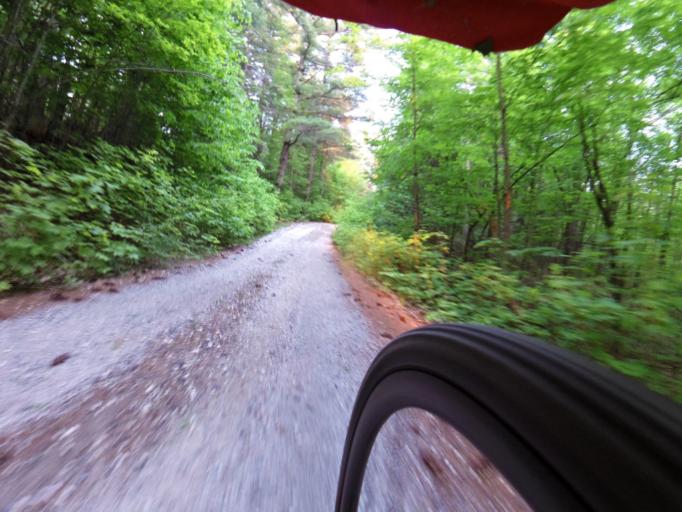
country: CA
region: Ontario
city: Arnprior
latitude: 45.1793
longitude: -76.5067
